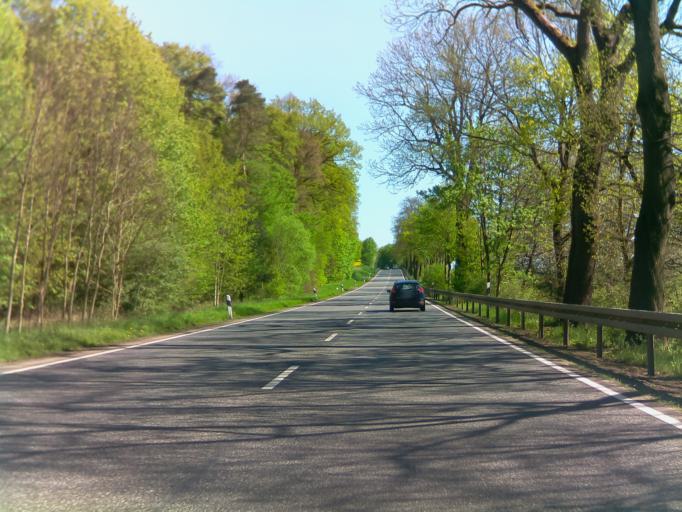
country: DE
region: Hesse
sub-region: Regierungsbezirk Giessen
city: Alsfeld
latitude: 50.7230
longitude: 9.2866
